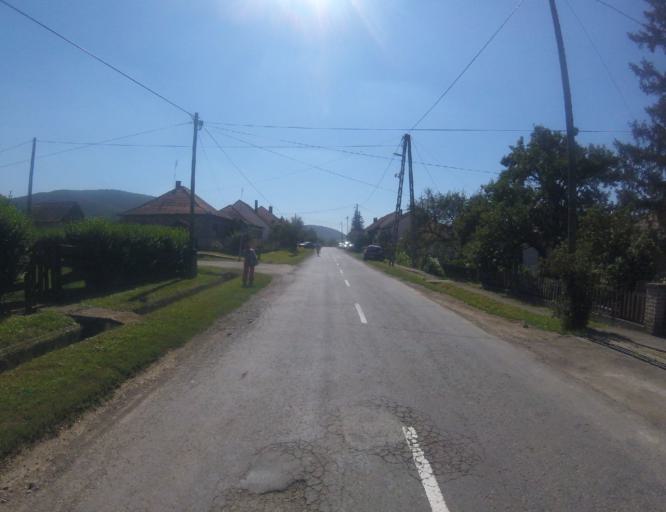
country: HU
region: Nograd
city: Bujak
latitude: 47.9503
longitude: 19.5940
